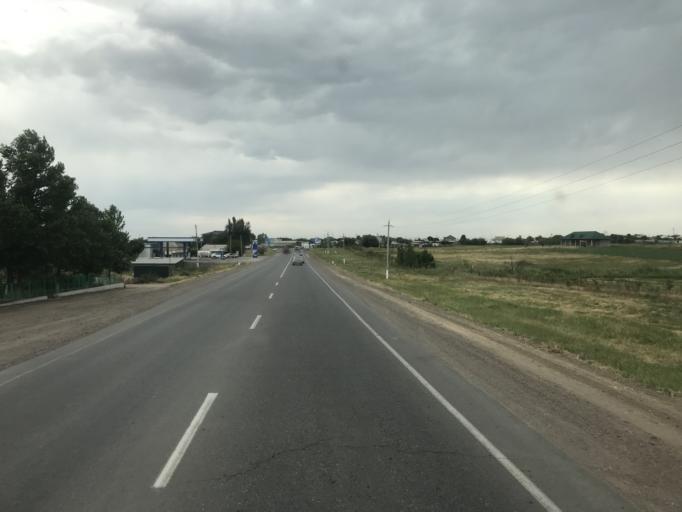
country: KZ
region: Ongtustik Qazaqstan
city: Saryaghash
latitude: 41.4350
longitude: 69.1156
